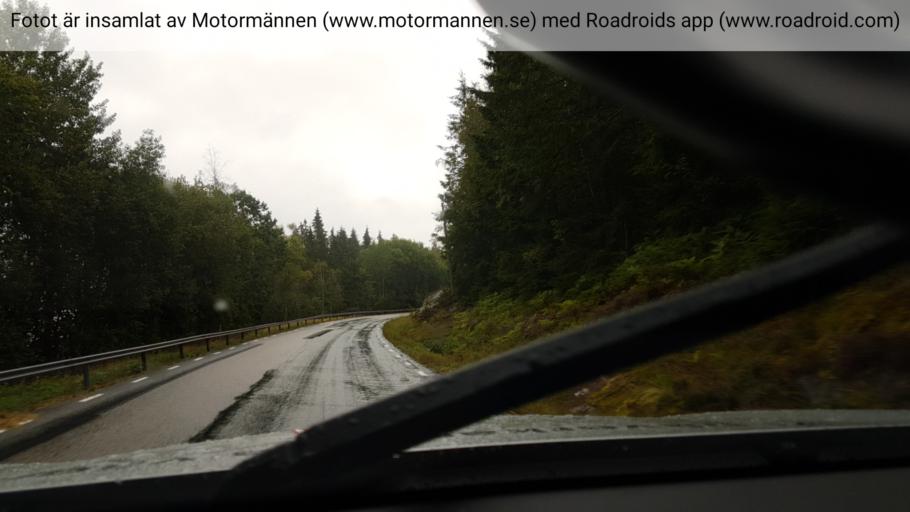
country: SE
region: Vaestra Goetaland
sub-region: Alingsas Kommun
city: Ingared
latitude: 57.8036
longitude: 12.5291
